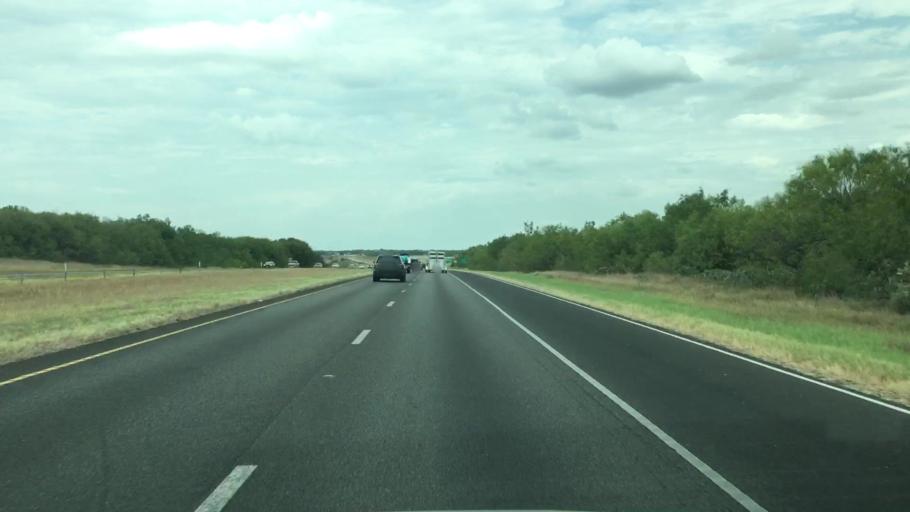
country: US
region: Texas
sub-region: Bexar County
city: Elmendorf
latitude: 29.1322
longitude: -98.4298
